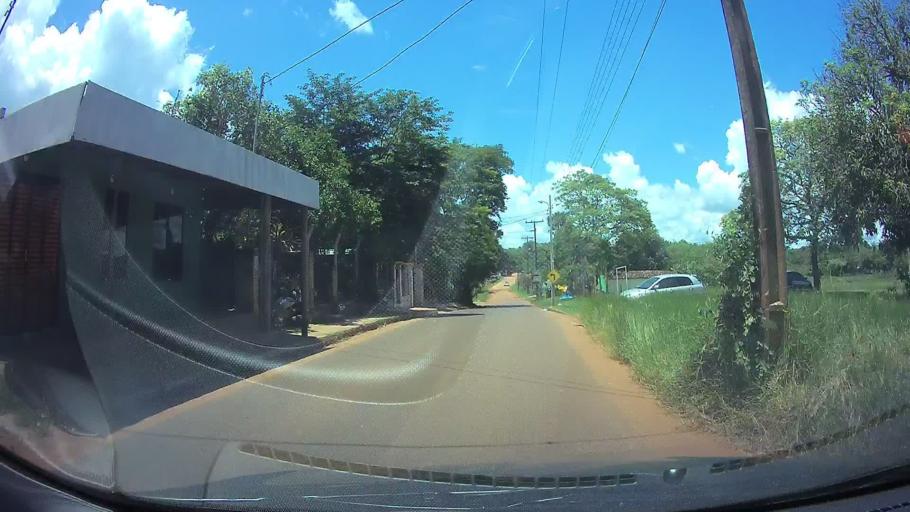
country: PY
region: Central
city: Itaugua
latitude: -25.3731
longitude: -57.3652
